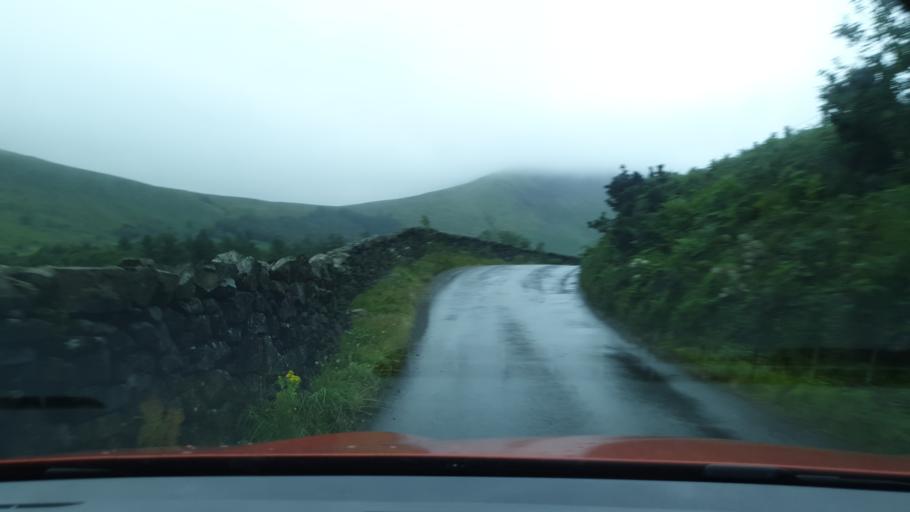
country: GB
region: England
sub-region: Cumbria
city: Keswick
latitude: 54.4594
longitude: -3.2633
